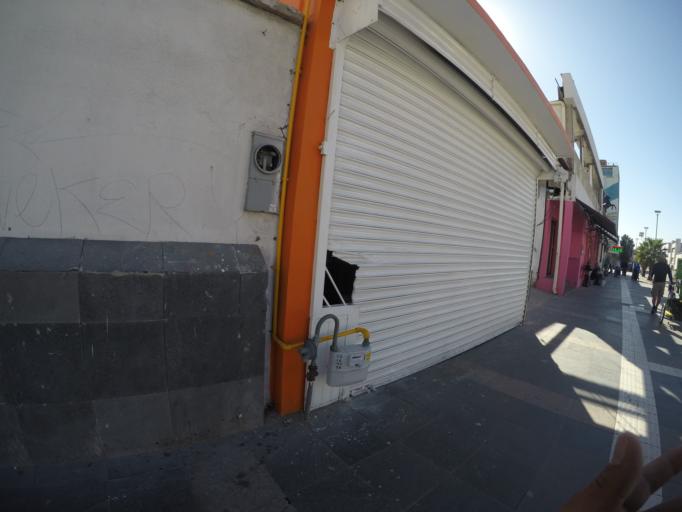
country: MX
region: Chihuahua
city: Ciudad Juarez
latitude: 31.7408
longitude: -106.4849
